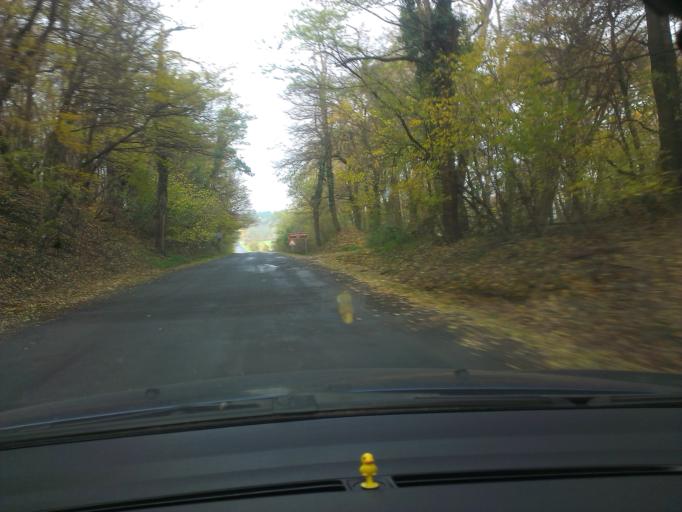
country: HU
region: Gyor-Moson-Sopron
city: Bakonyszentlaszlo
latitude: 47.3775
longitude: 17.8538
